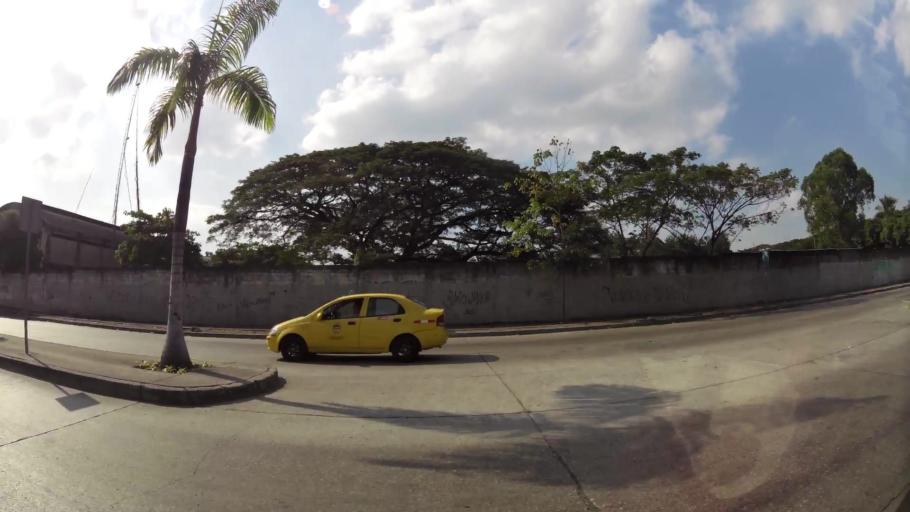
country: EC
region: Guayas
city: Guayaquil
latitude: -2.1308
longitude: -79.9318
